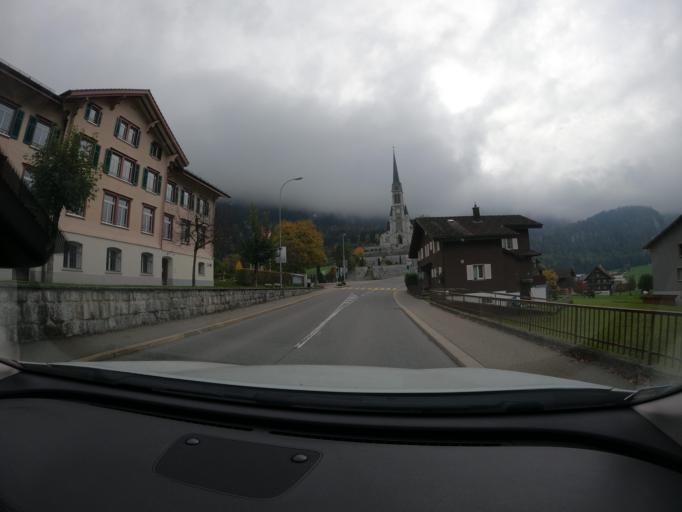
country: CH
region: Obwalden
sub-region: Obwalden
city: Lungern
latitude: 46.7839
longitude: 8.1591
